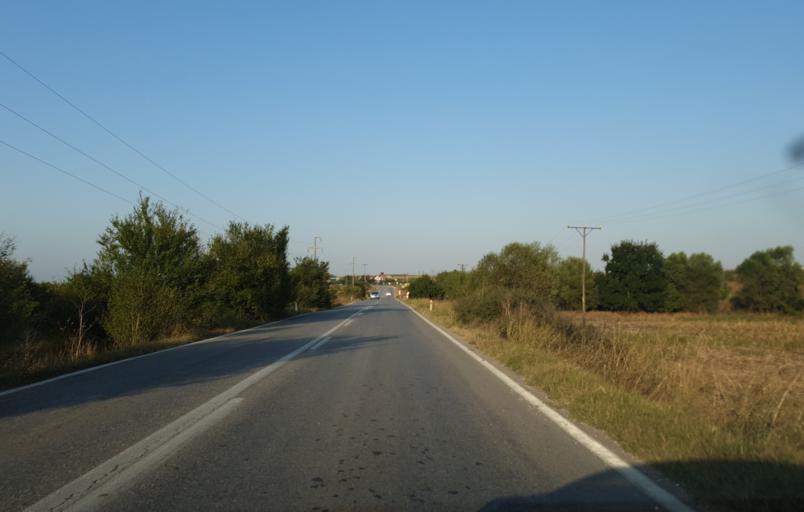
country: TR
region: Tekirdag
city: Saray
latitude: 41.4305
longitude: 27.8902
